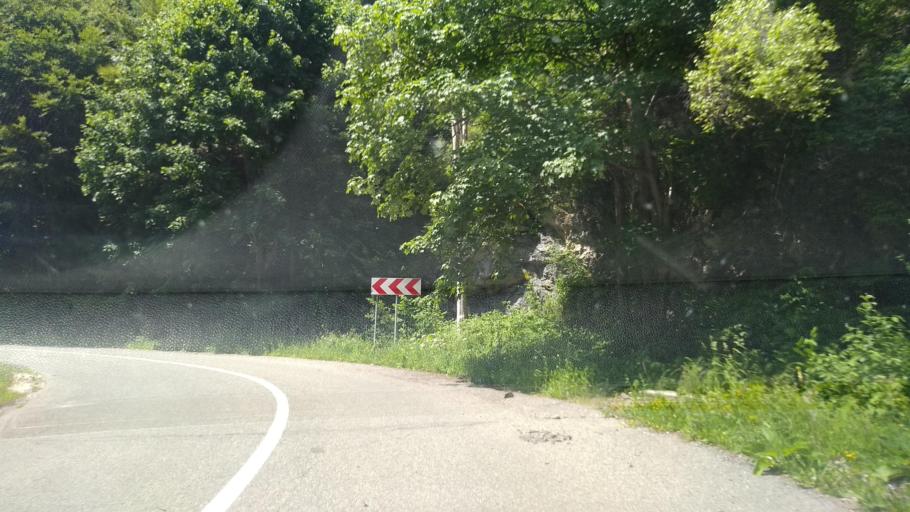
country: RO
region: Hunedoara
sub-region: Comuna Uricani
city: Uricani
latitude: 45.2785
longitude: 22.9627
